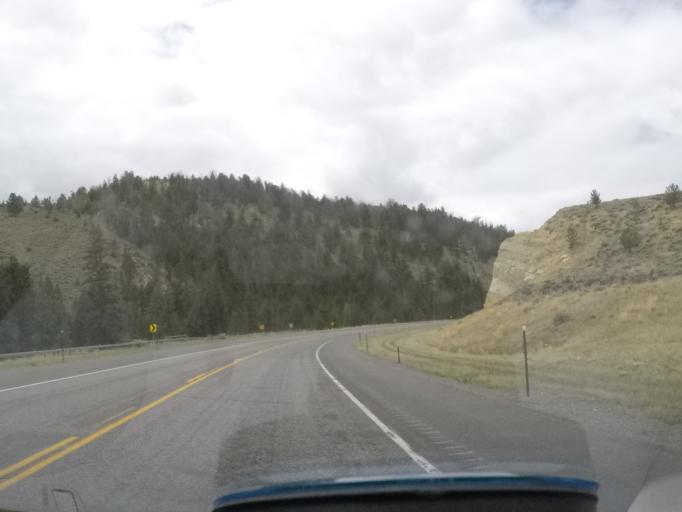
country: US
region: Wyoming
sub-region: Sublette County
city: Pinedale
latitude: 43.5788
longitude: -109.7587
